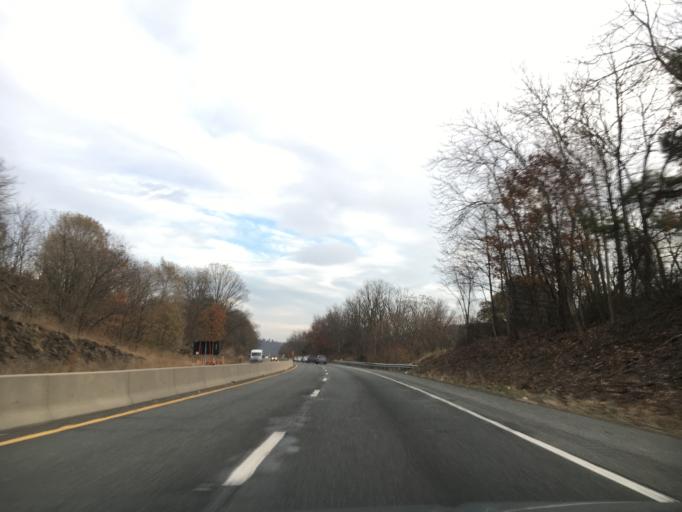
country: US
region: Pennsylvania
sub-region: Carbon County
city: Weissport East
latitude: 40.8249
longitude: -75.6949
